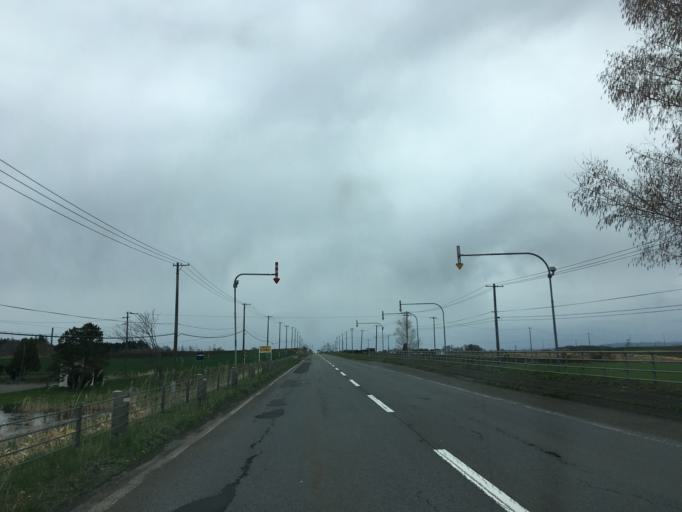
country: JP
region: Hokkaido
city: Chitose
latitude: 42.9205
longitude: 141.8090
